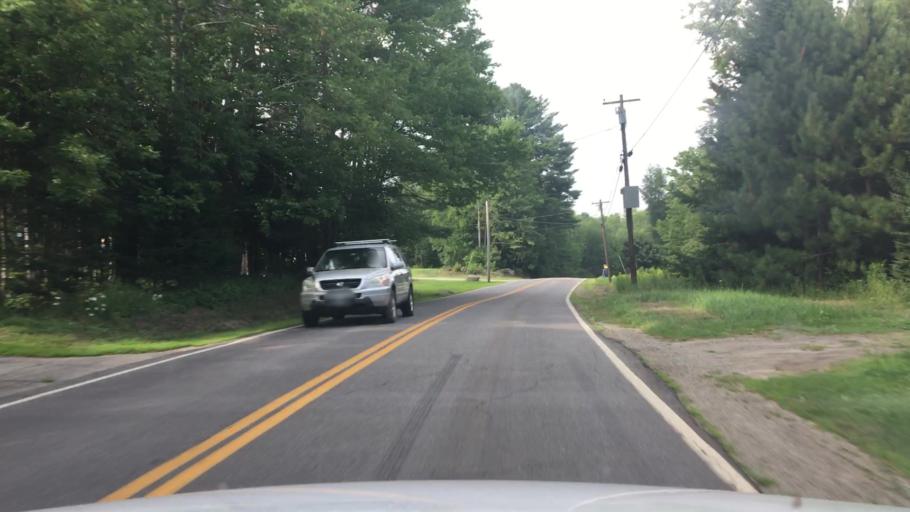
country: US
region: Maine
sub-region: Lincoln County
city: Waldoboro
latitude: 44.1742
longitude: -69.3788
